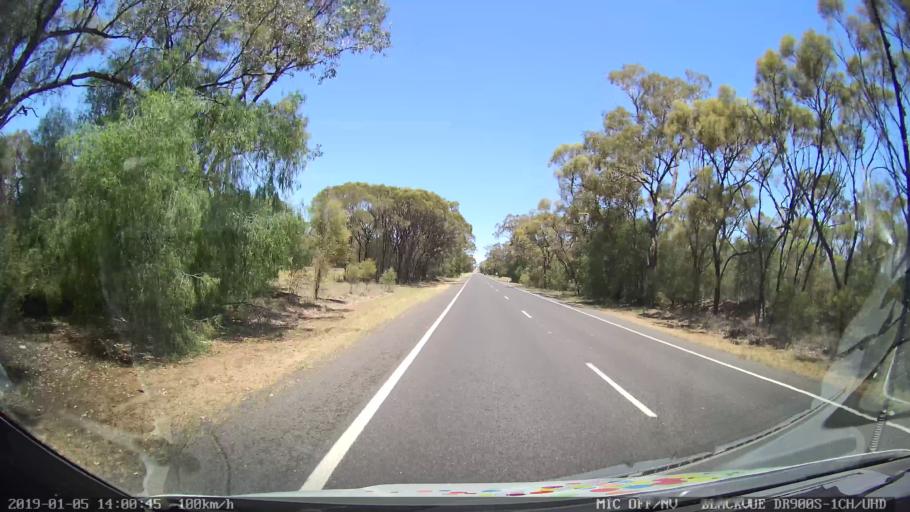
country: AU
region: New South Wales
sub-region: Gunnedah
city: Gunnedah
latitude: -31.1628
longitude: 150.3163
